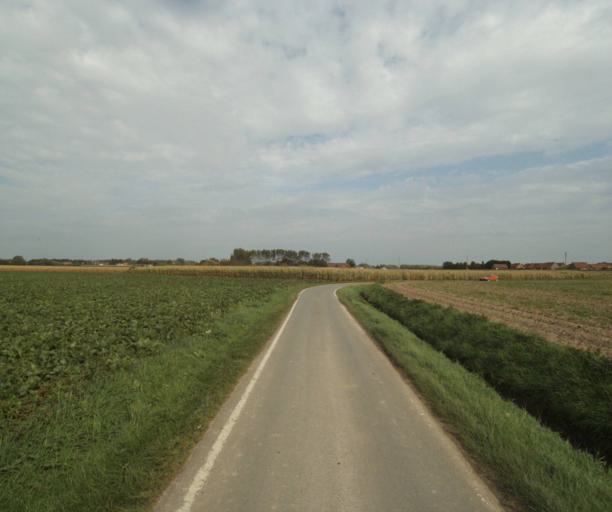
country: FR
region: Nord-Pas-de-Calais
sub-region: Departement du Nord
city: Marquillies
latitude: 50.5411
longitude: 2.8678
